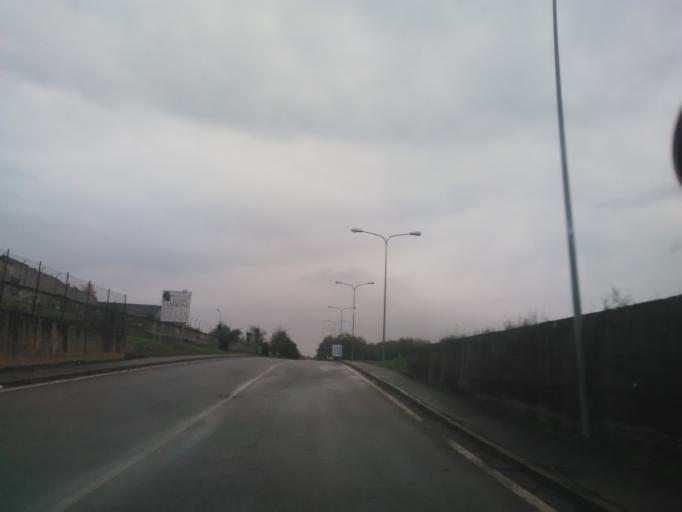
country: IT
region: Piedmont
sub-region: Provincia di Vercelli
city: Gattinara
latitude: 45.6077
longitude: 8.3636
